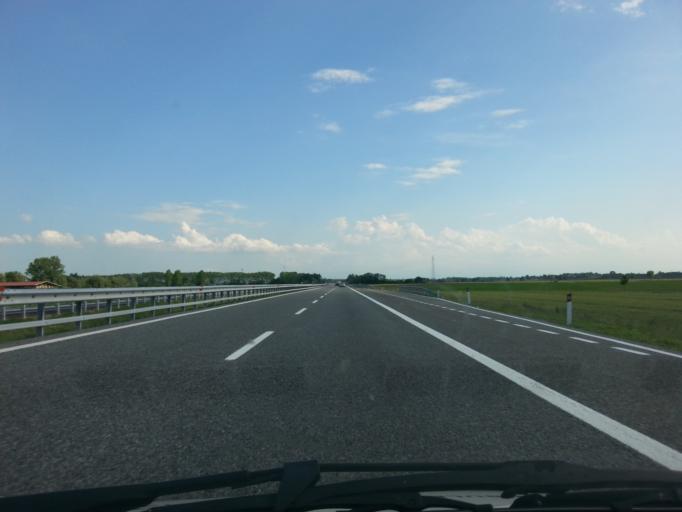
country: IT
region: Piedmont
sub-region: Provincia di Cuneo
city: Sommariva del Bosco
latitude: 44.7306
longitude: 7.7554
